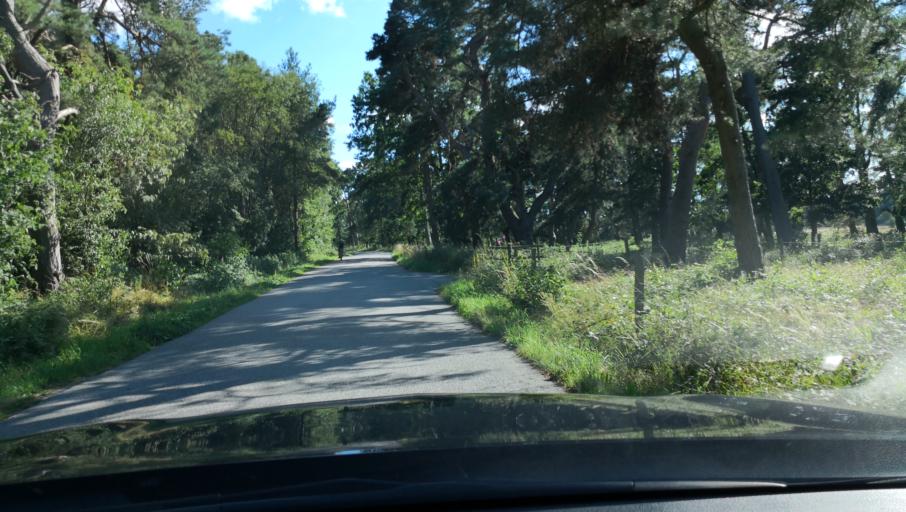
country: SE
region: Skane
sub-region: Simrishamns Kommun
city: Kivik
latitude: 55.7886
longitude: 14.1968
